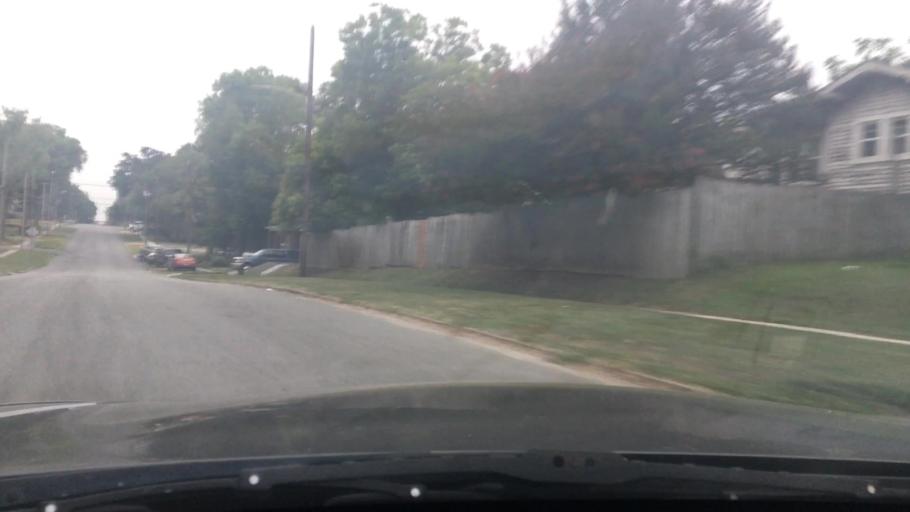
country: US
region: North Carolina
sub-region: Alamance County
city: Burlington
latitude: 36.0975
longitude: -79.4294
